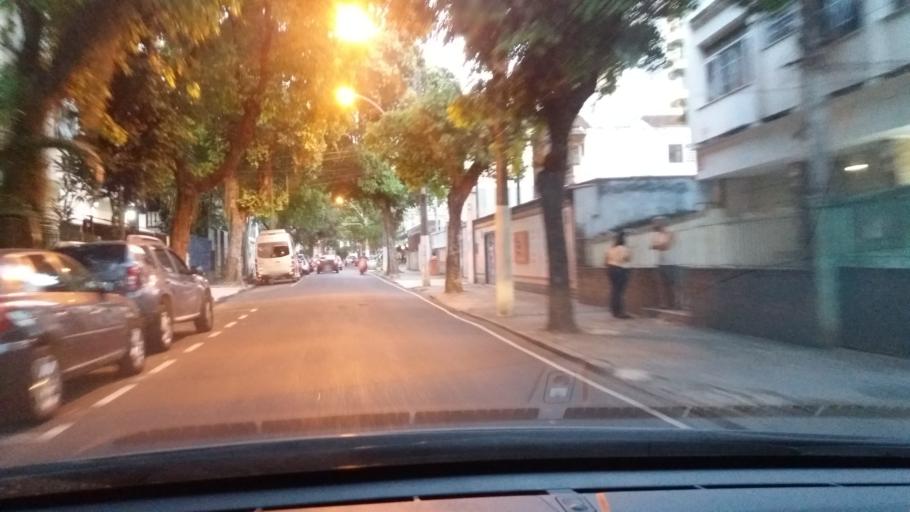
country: BR
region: Rio de Janeiro
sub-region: Niteroi
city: Niteroi
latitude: -22.9018
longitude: -43.1015
